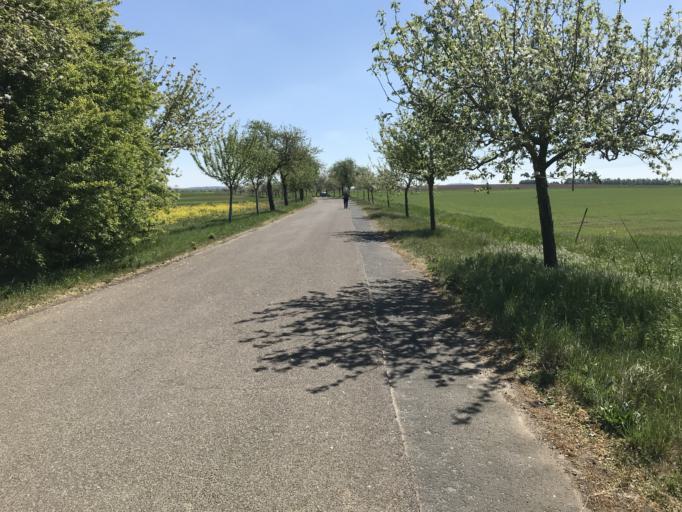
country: DE
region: Bavaria
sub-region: Regierungsbezirk Unterfranken
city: Iphofen
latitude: 49.6926
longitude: 10.2615
